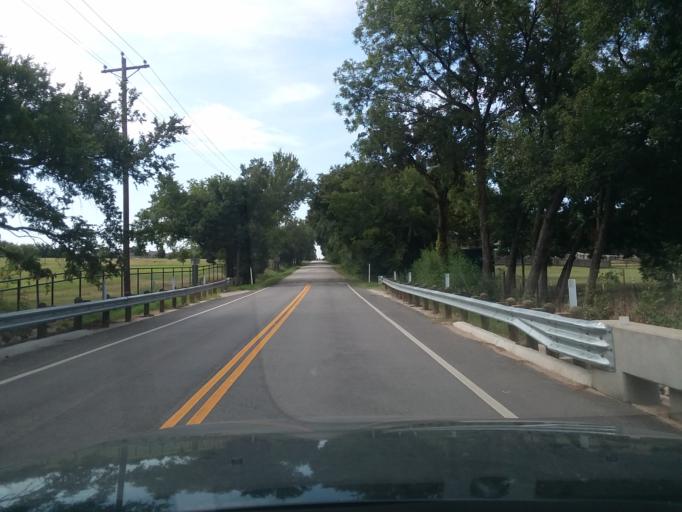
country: US
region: Texas
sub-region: Denton County
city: Bartonville
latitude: 33.1079
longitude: -97.1312
